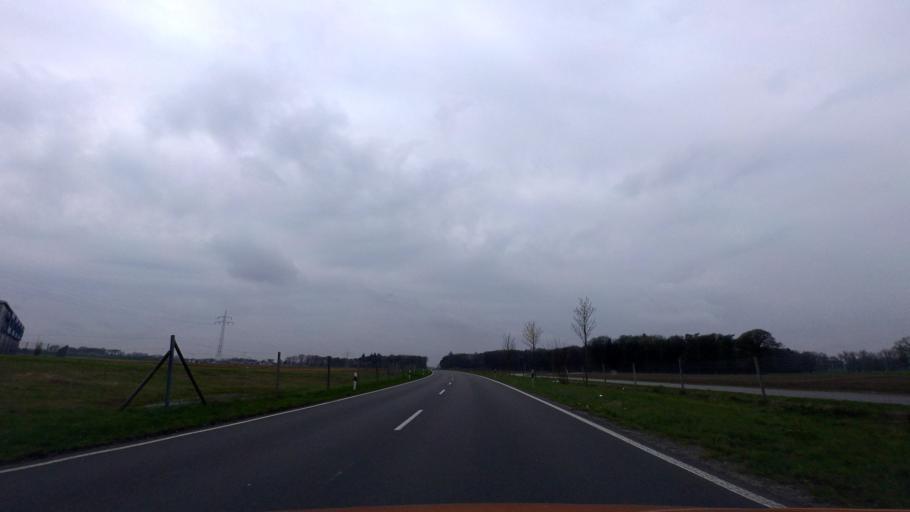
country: DE
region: Lower Saxony
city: Vechta
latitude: 52.7507
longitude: 8.2658
